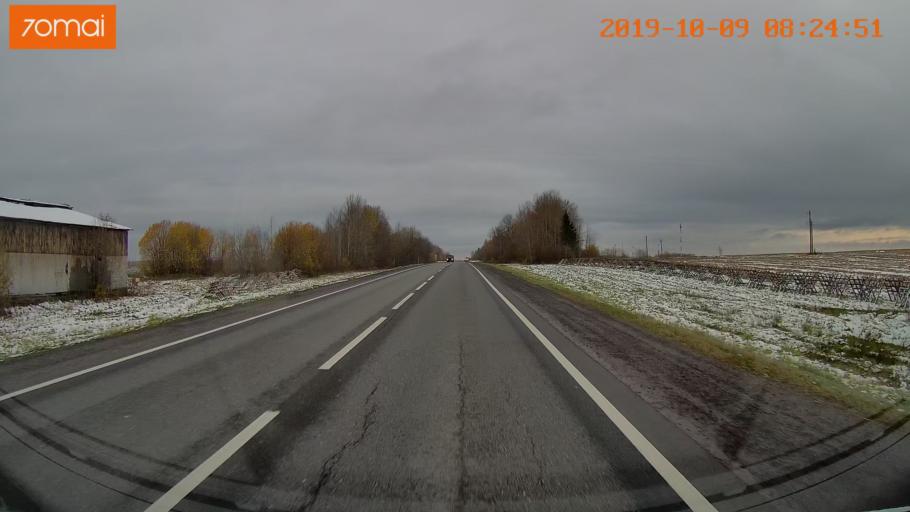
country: RU
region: Vologda
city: Gryazovets
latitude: 58.7723
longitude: 40.2759
